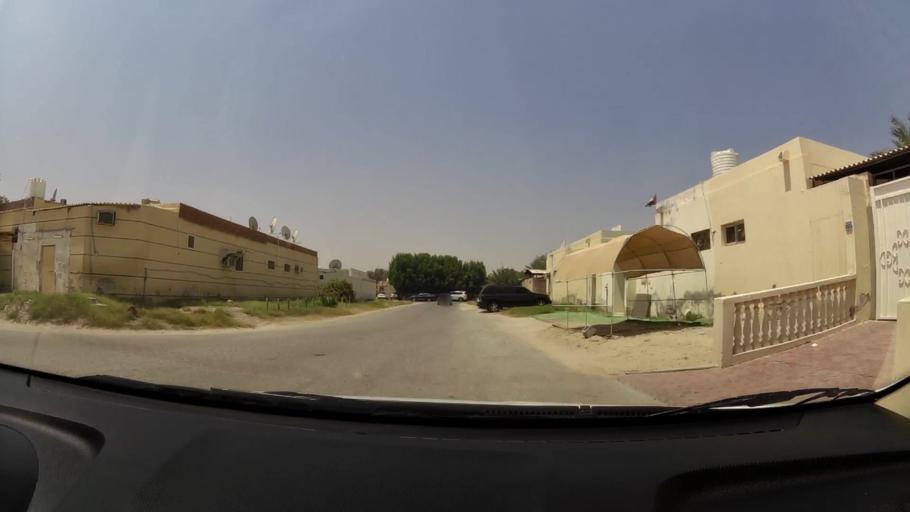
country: AE
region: Umm al Qaywayn
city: Umm al Qaywayn
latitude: 25.5606
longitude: 55.5598
